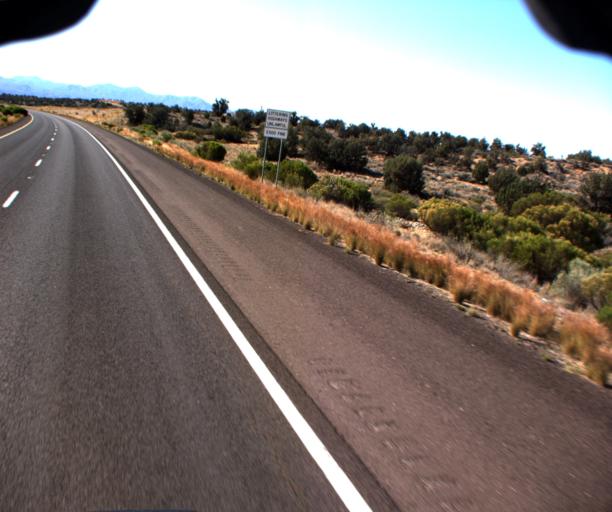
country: US
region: Arizona
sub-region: Mohave County
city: New Kingman-Butler
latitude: 35.1471
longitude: -113.6877
